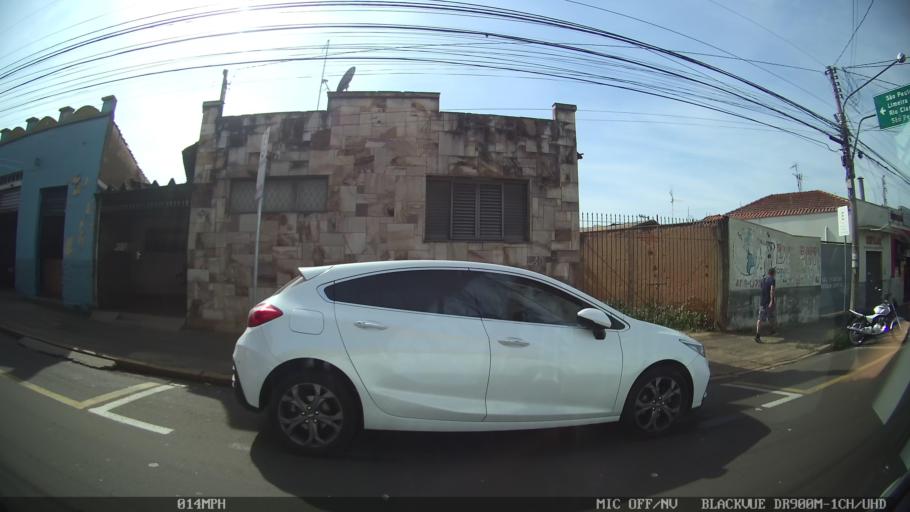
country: BR
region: Sao Paulo
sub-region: Piracicaba
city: Piracicaba
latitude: -22.7395
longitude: -47.6530
